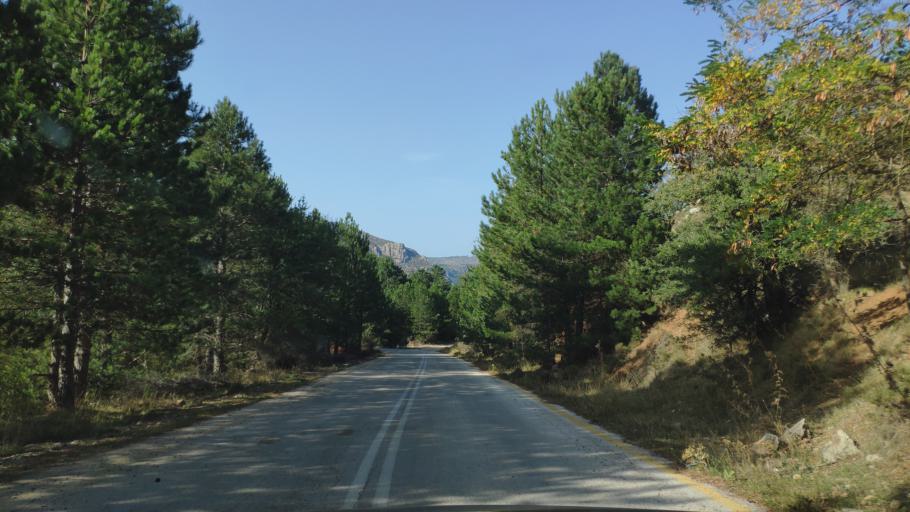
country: GR
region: West Greece
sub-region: Nomos Achaias
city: Aiyira
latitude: 38.0557
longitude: 22.3818
